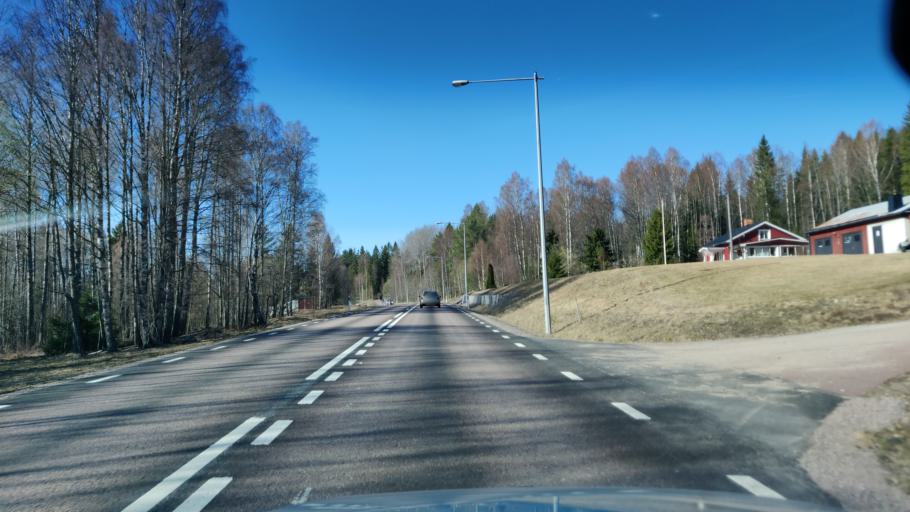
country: SE
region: Vaermland
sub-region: Hagfors Kommun
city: Hagfors
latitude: 59.9427
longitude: 13.6770
